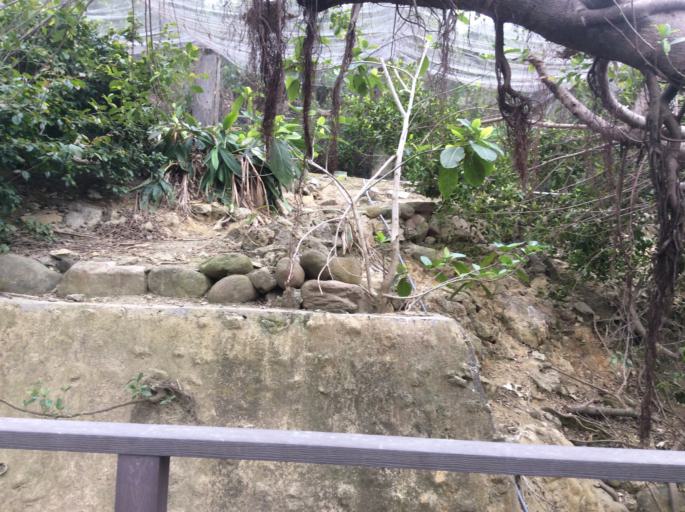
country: TW
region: Kaohsiung
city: Kaohsiung
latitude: 22.6376
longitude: 120.2752
